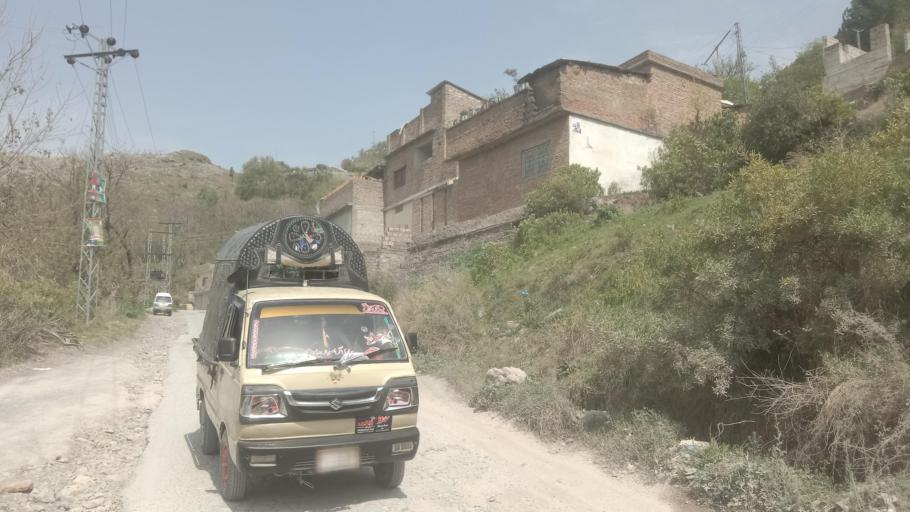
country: PK
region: Khyber Pakhtunkhwa
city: Abbottabad
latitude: 34.1655
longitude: 73.2821
